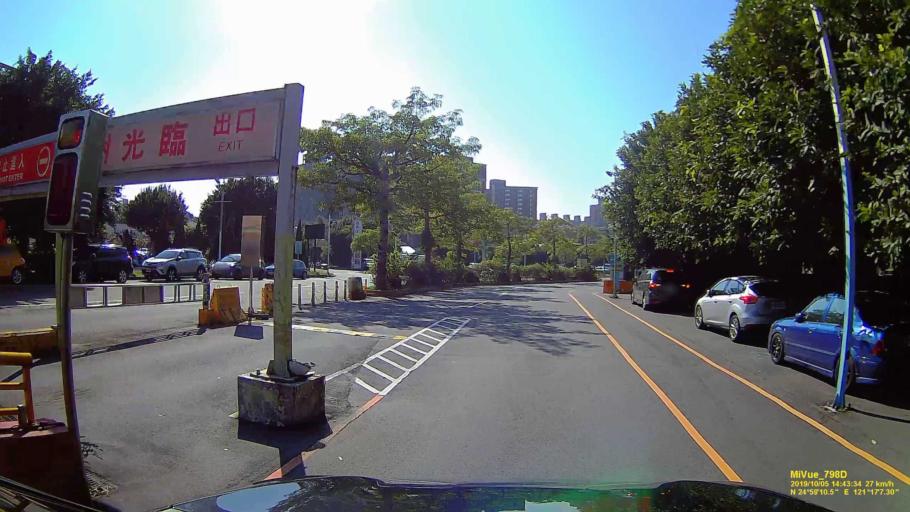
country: TW
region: Taiwan
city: Taoyuan City
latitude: 24.9862
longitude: 121.2852
